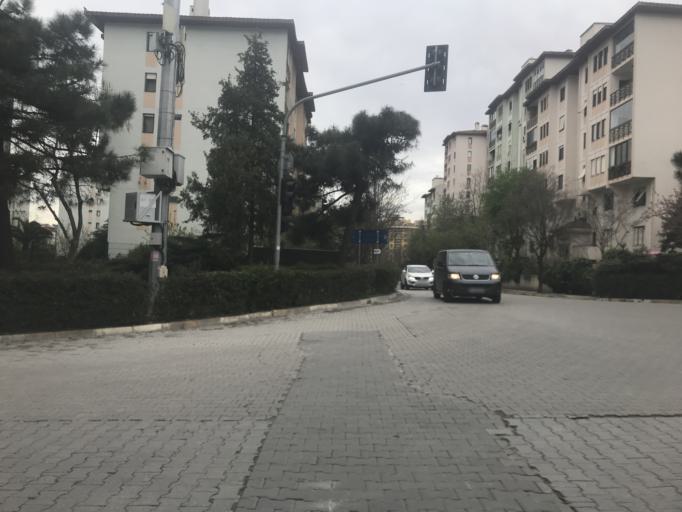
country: TR
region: Istanbul
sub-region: Atasehir
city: Atasehir
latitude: 40.9915
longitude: 29.1322
